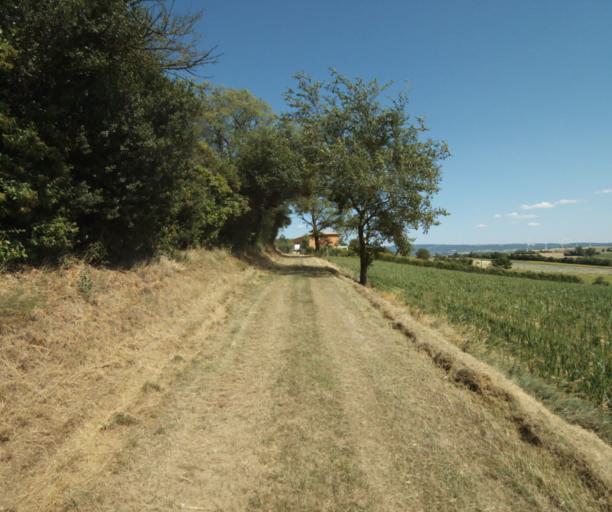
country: FR
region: Midi-Pyrenees
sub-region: Departement de la Haute-Garonne
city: Saint-Felix-Lauragais
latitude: 43.4879
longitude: 1.8980
